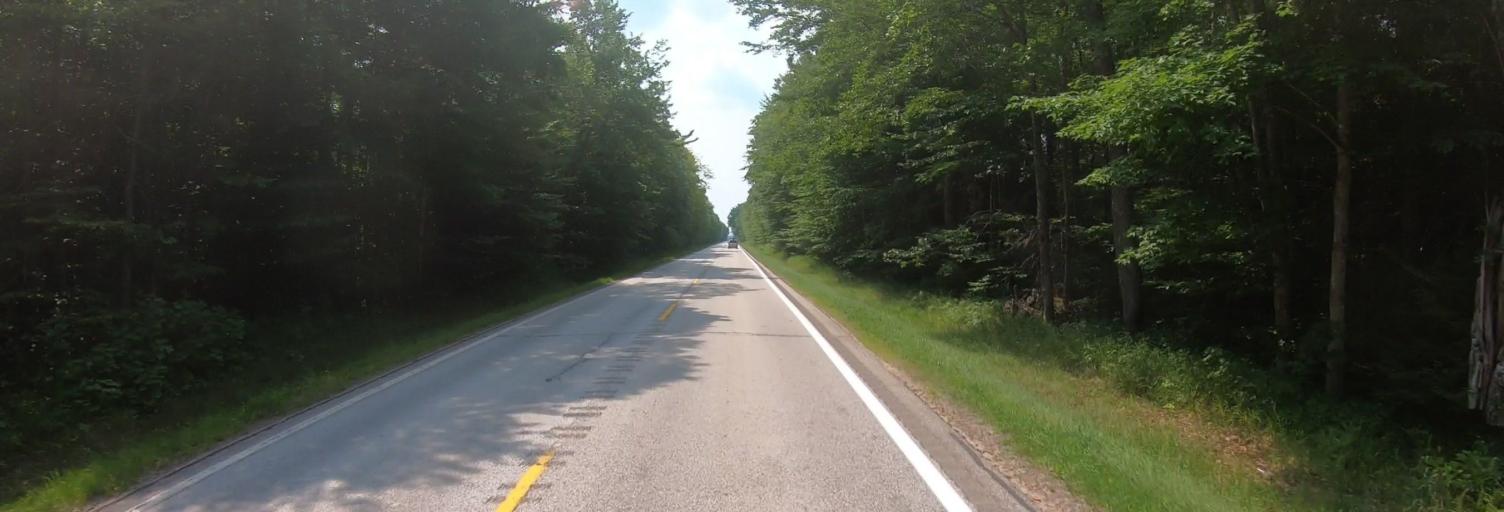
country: US
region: Michigan
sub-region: Luce County
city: Newberry
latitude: 46.5011
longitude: -85.4267
